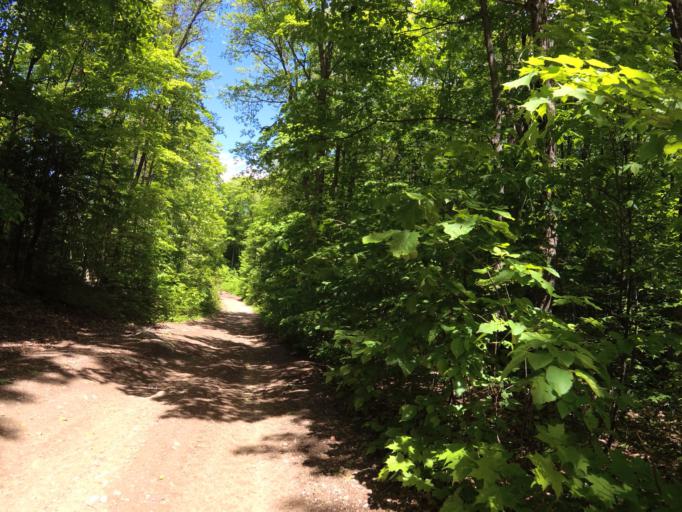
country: CA
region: Ontario
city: Renfrew
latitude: 45.0275
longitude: -76.8846
